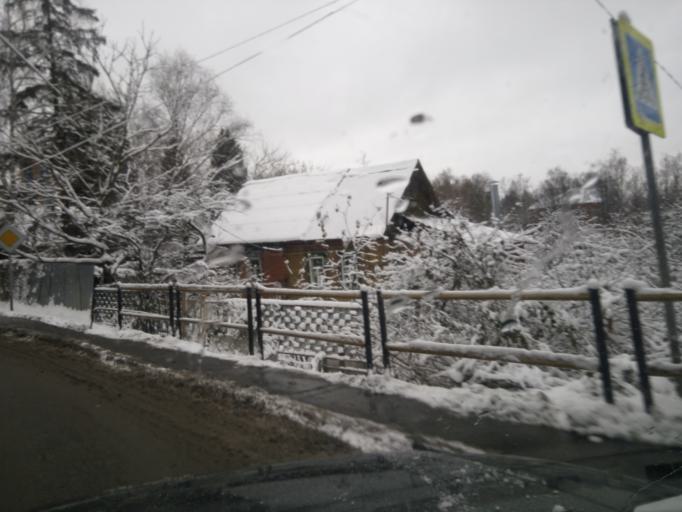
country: RU
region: Moskovskaya
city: Skhodnya
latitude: 55.9509
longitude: 37.3109
